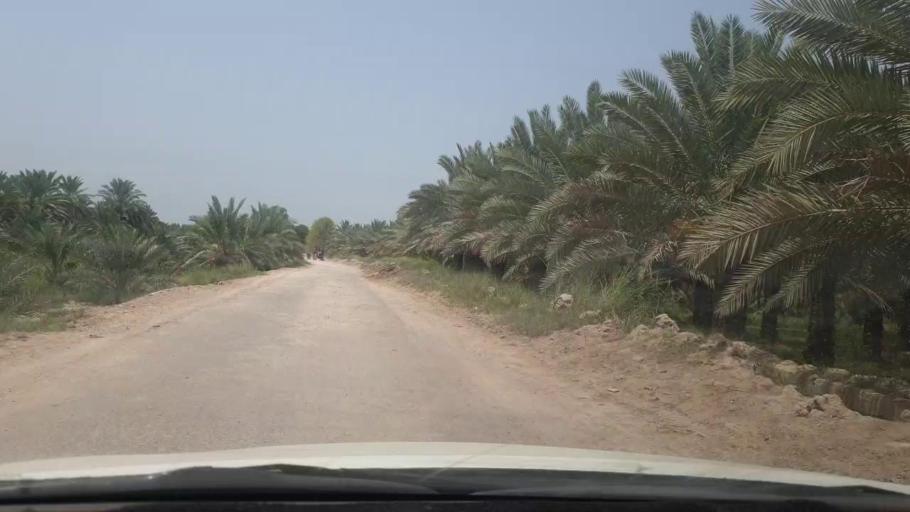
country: PK
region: Sindh
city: Khairpur
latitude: 27.5028
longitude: 68.8670
